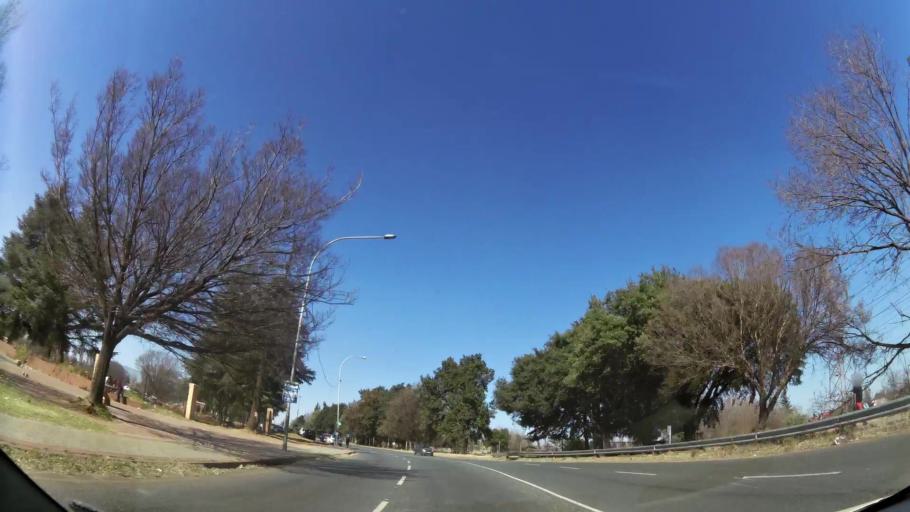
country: ZA
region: Gauteng
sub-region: City of Johannesburg Metropolitan Municipality
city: Johannesburg
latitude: -26.1928
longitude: 27.9589
